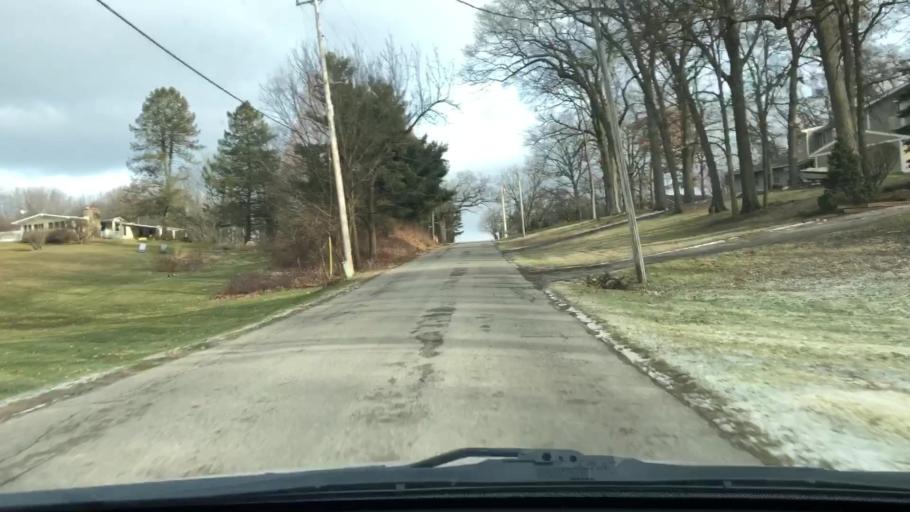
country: US
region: Indiana
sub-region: Steuben County
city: Angola
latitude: 41.6826
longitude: -85.0086
